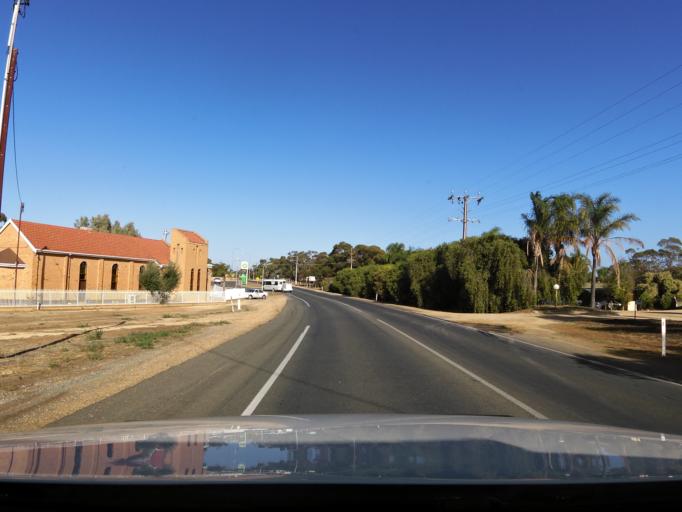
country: AU
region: South Australia
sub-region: Berri and Barmera
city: Berri
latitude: -34.2708
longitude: 140.6088
